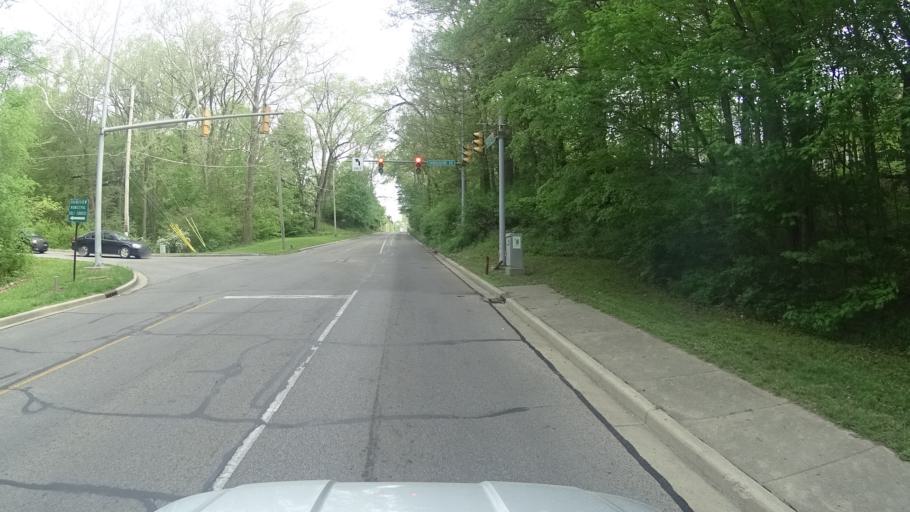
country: US
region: Indiana
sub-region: Madison County
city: Anderson
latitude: 40.1197
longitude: -85.6917
